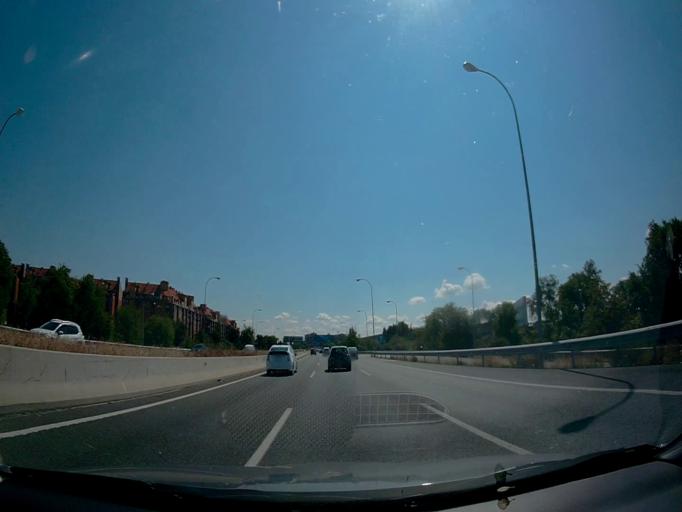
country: ES
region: Madrid
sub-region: Provincia de Madrid
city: Villaverde
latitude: 40.3640
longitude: -3.7126
